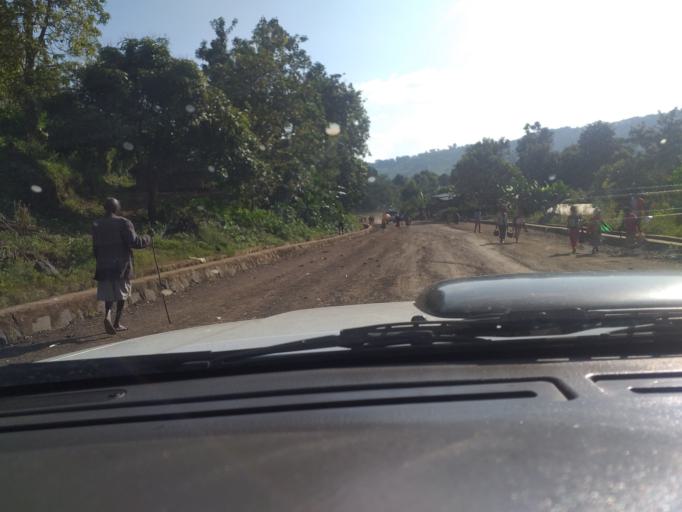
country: ET
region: Southern Nations, Nationalities, and People's Region
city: Bako
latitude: 5.9806
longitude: 36.5735
